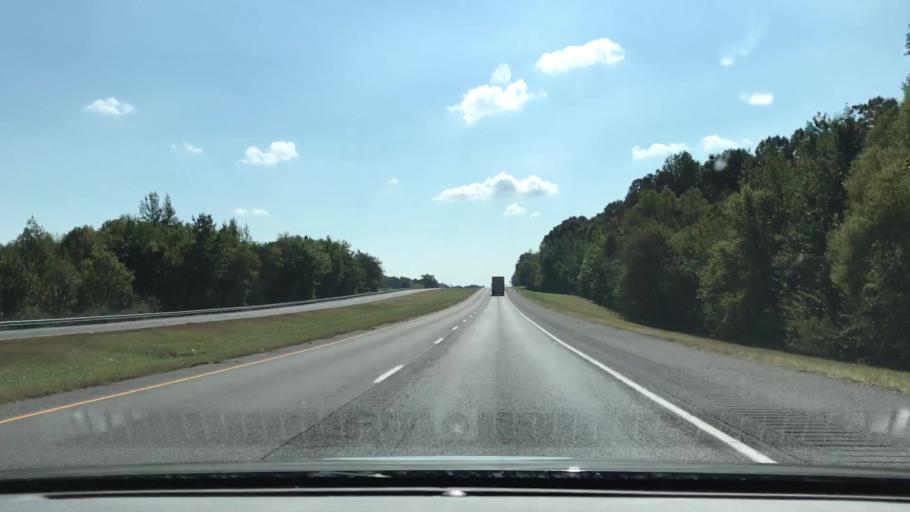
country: US
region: Kentucky
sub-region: Marshall County
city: Benton
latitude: 36.7740
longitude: -88.3183
